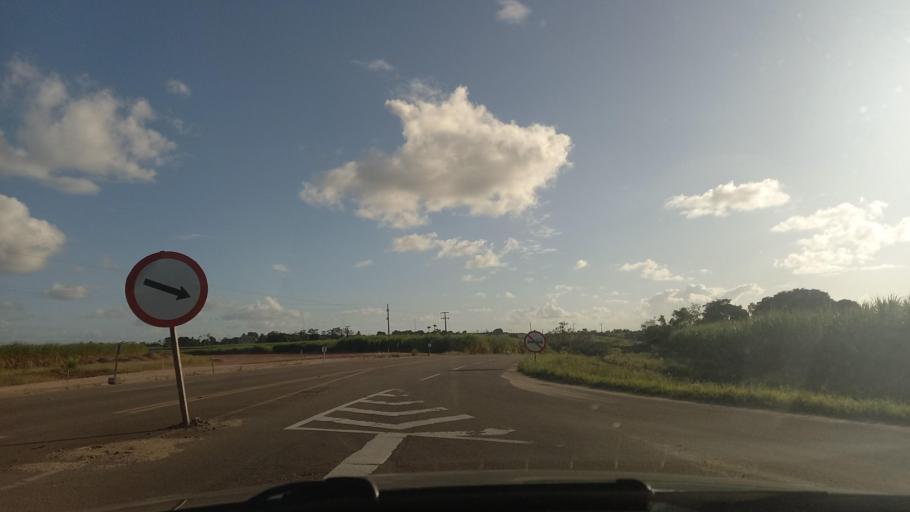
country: BR
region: Alagoas
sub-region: Sao Miguel Dos Campos
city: Sao Miguel dos Campos
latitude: -9.8039
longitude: -36.2006
